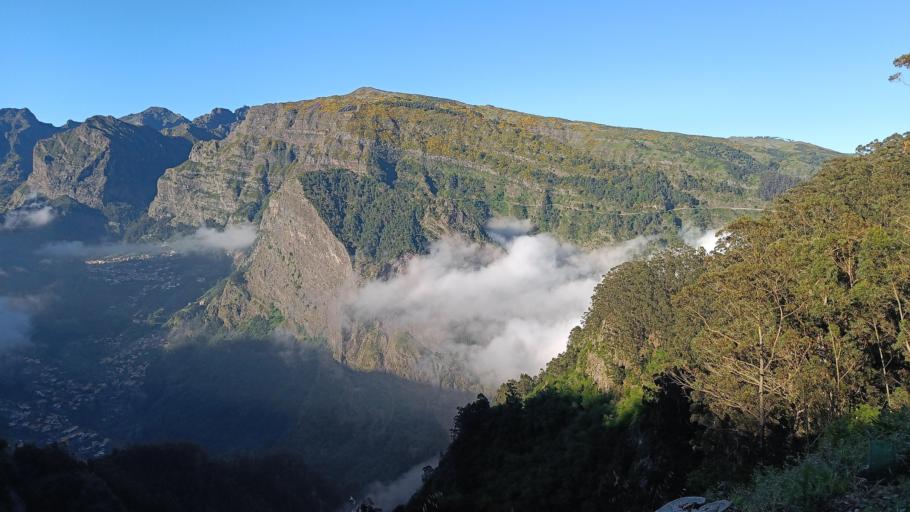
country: PT
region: Madeira
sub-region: Camara de Lobos
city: Curral das Freiras
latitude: 32.6956
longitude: -16.9783
